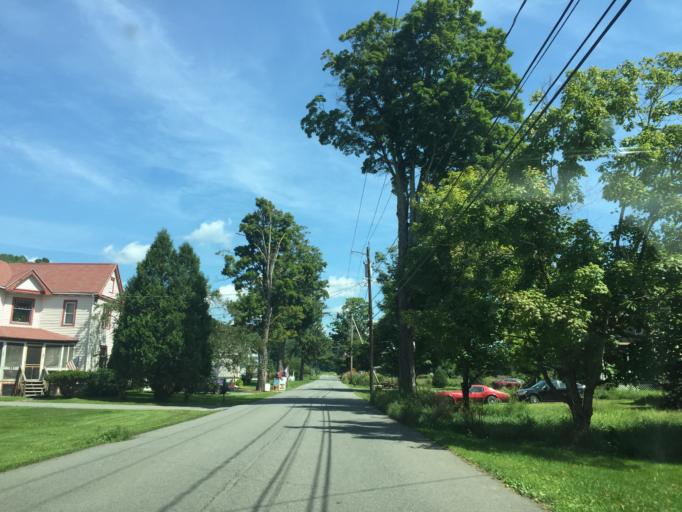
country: US
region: New York
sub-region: Delaware County
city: Walton
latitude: 42.0858
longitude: -74.9933
